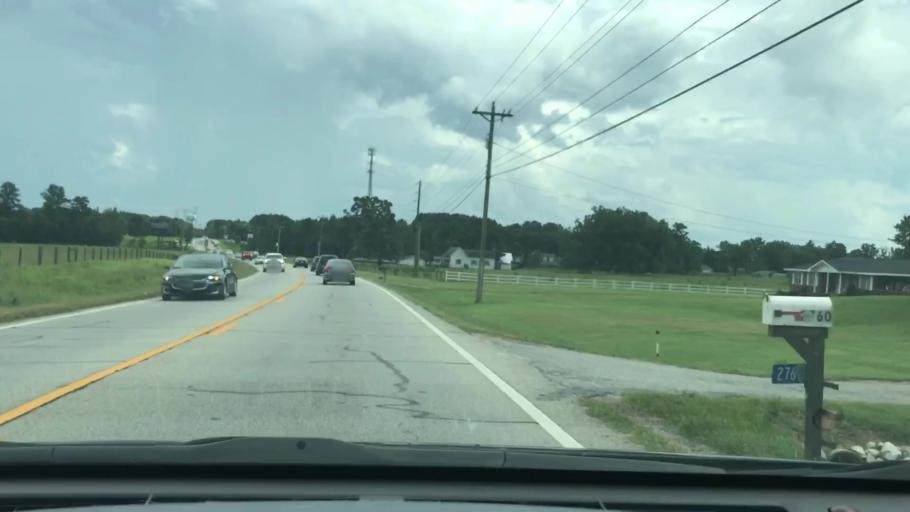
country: US
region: Georgia
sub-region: Walton County
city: Loganville
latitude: 33.8005
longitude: -83.8709
